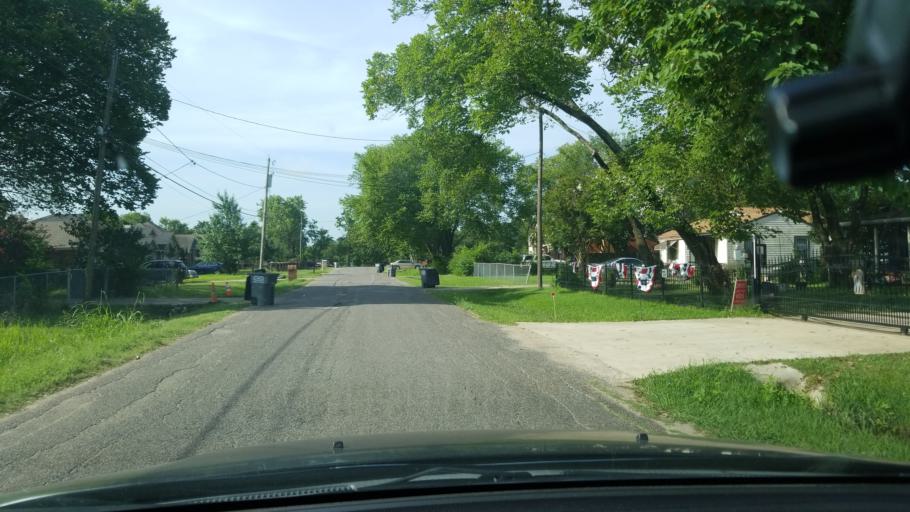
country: US
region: Texas
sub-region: Dallas County
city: Balch Springs
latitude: 32.7136
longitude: -96.6364
